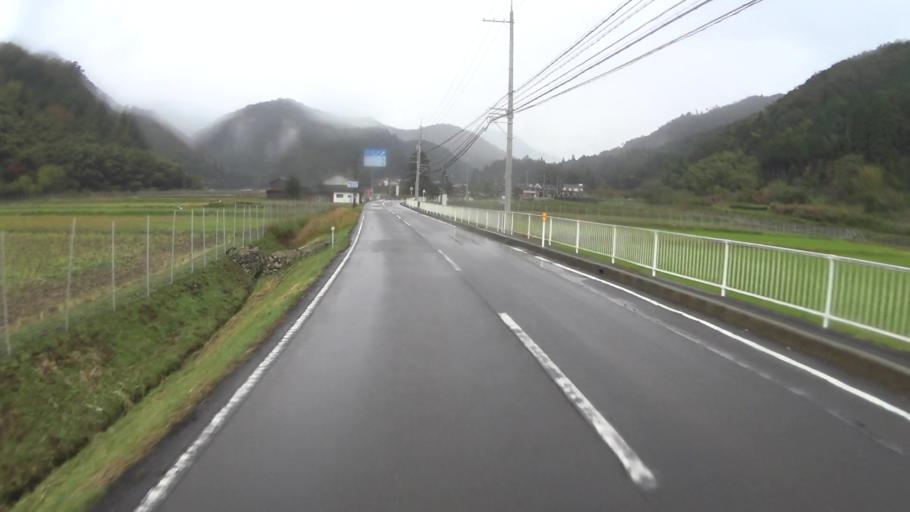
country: JP
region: Kyoto
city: Miyazu
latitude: 35.4221
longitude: 135.1568
